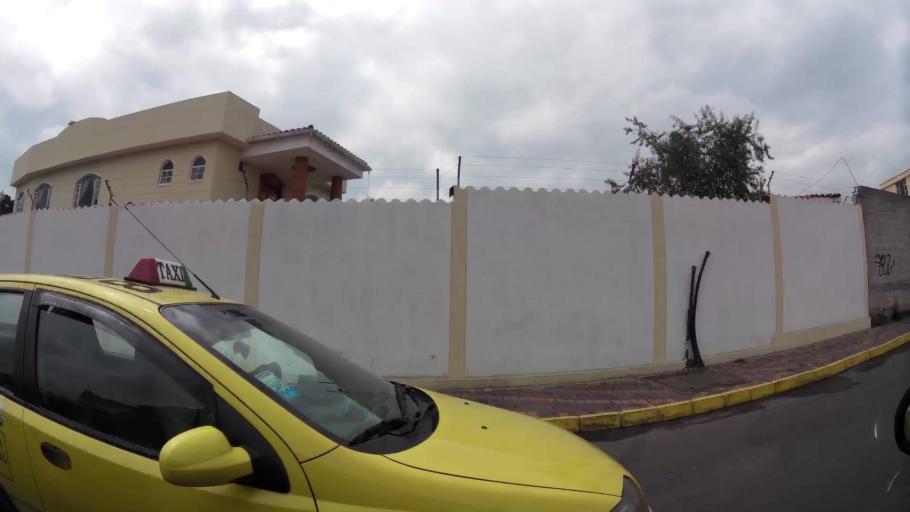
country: EC
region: Pichincha
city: Sangolqui
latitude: -0.3128
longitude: -78.4731
